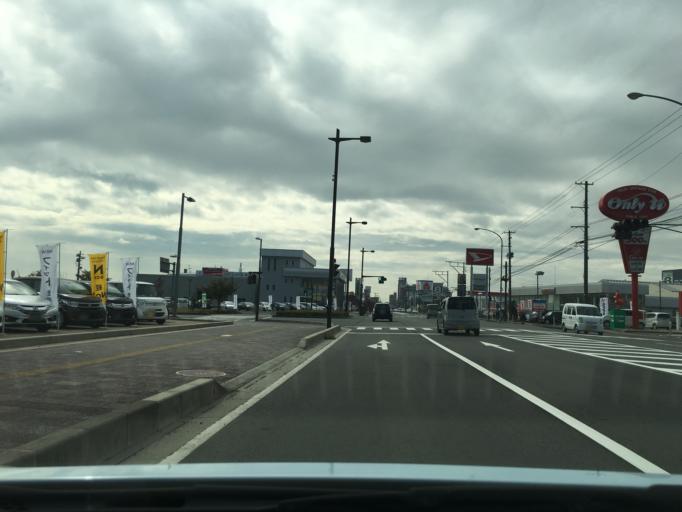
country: JP
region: Fukushima
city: Koriyama
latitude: 37.3716
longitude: 140.3723
